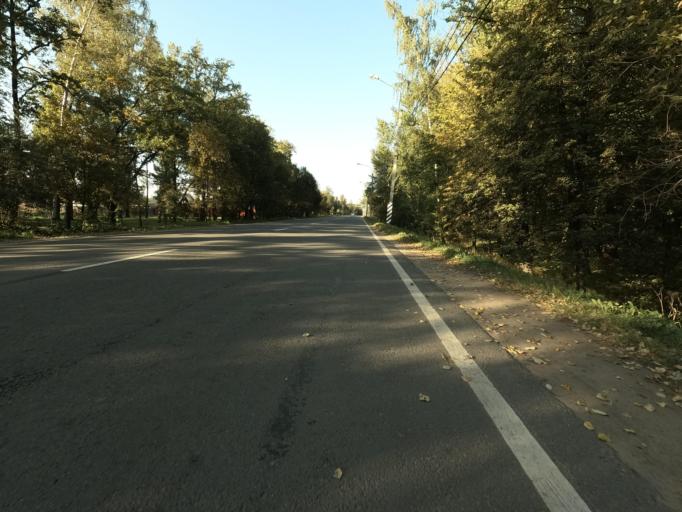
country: RU
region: St.-Petersburg
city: Kolpino
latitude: 59.7513
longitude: 30.6159
